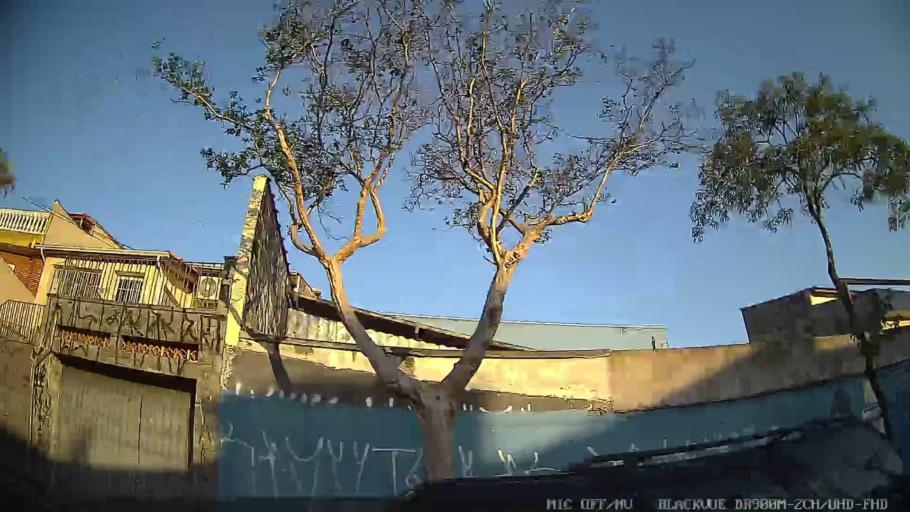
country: BR
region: Sao Paulo
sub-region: Sao Caetano Do Sul
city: Sao Caetano do Sul
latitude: -23.5790
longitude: -46.5491
